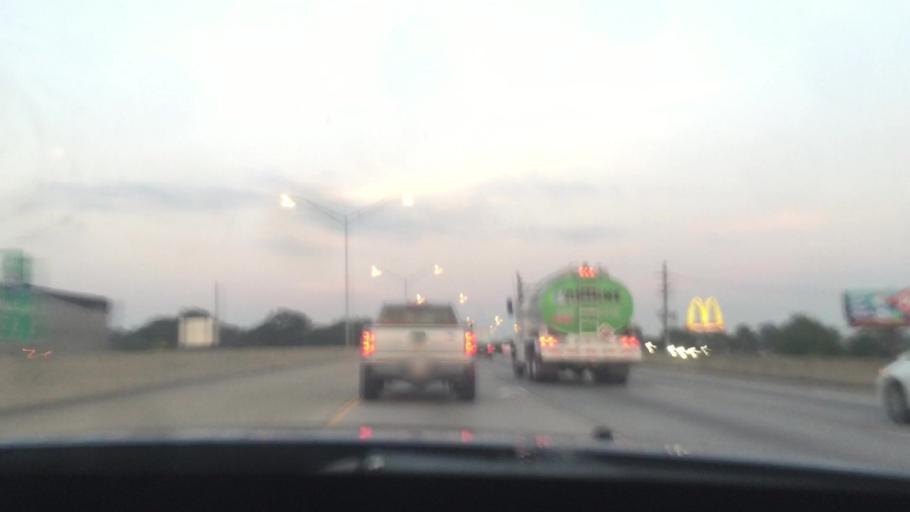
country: US
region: Louisiana
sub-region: East Baton Rouge Parish
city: Westminster
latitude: 30.4183
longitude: -91.0881
